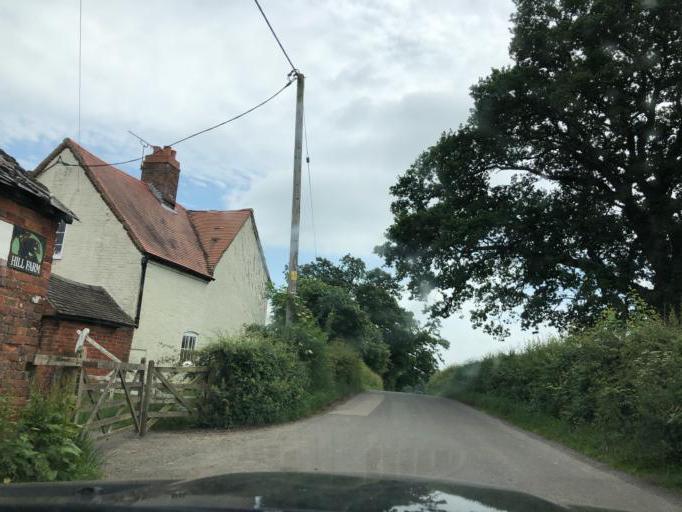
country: GB
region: England
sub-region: Warwickshire
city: Wroxall
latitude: 52.3348
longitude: -1.6416
